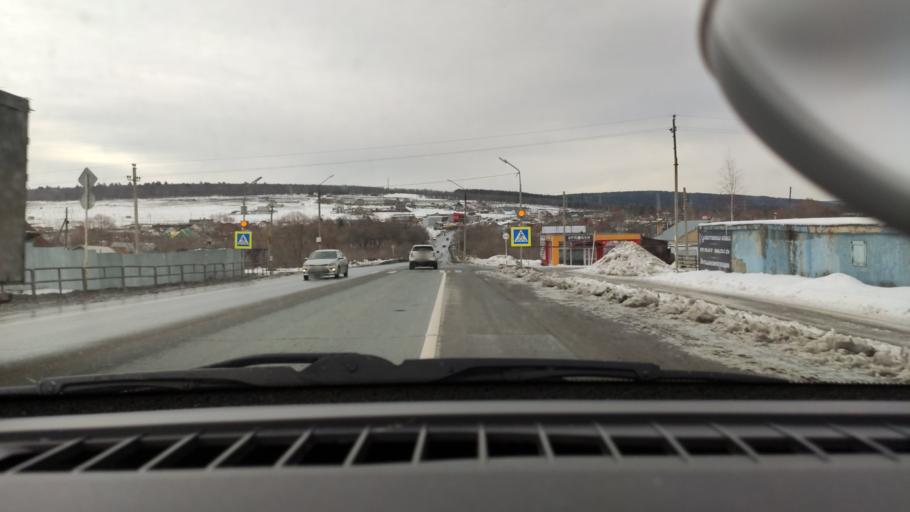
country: RU
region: Samara
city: Kurumoch
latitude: 53.4830
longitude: 50.0389
